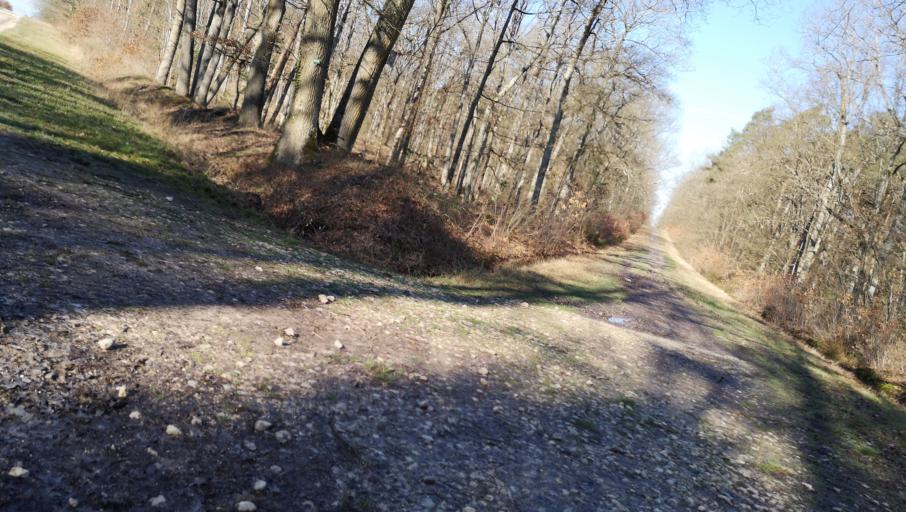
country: FR
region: Centre
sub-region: Departement du Loiret
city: Chanteau
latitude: 47.9514
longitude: 1.9730
